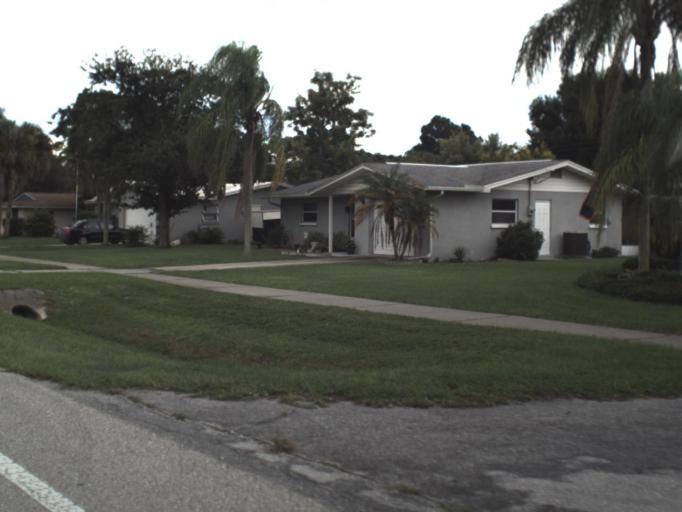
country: US
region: Florida
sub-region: Sarasota County
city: Venice Gardens
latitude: 27.0997
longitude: -82.4192
